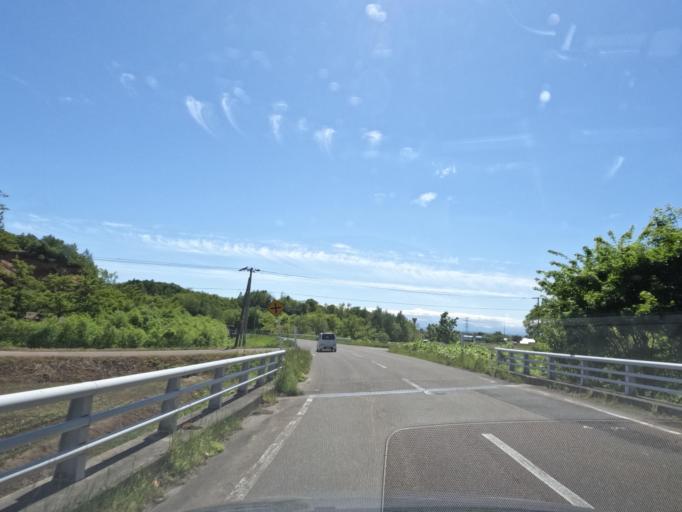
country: JP
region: Hokkaido
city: Iwamizawa
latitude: 43.0892
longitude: 141.7545
